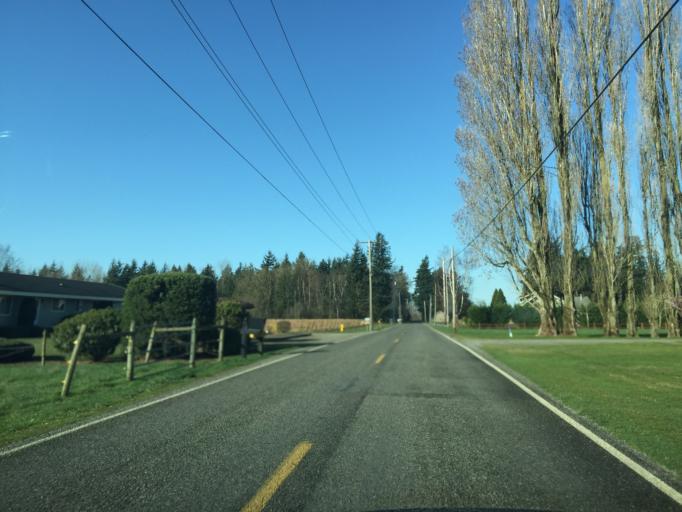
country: US
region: Washington
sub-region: Whatcom County
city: Lynden
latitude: 48.9062
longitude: -122.5048
